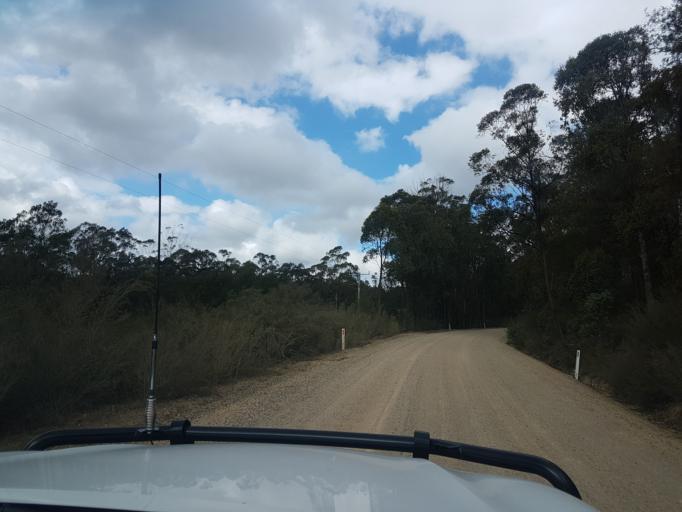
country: AU
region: Victoria
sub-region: East Gippsland
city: Bairnsdale
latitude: -37.6810
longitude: 147.5537
